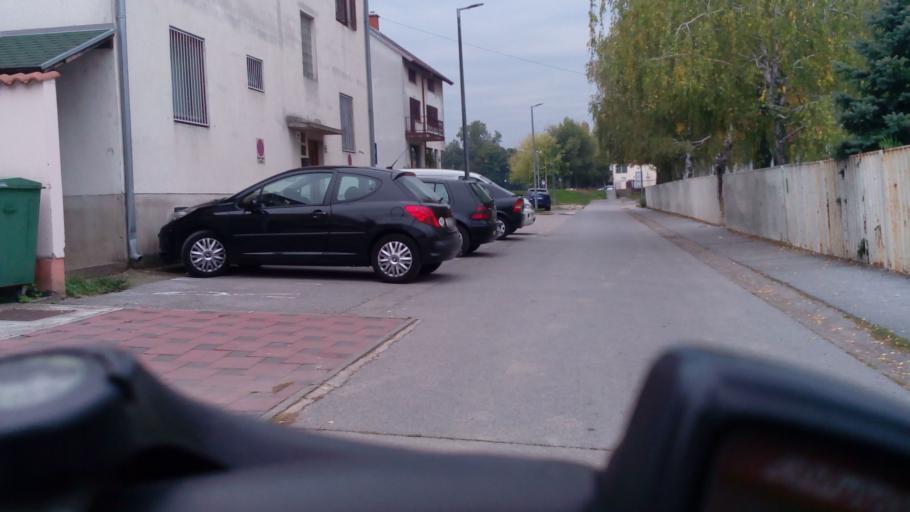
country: HR
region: Vukovarsko-Srijemska
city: Vinkovci
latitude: 45.2871
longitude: 18.8054
